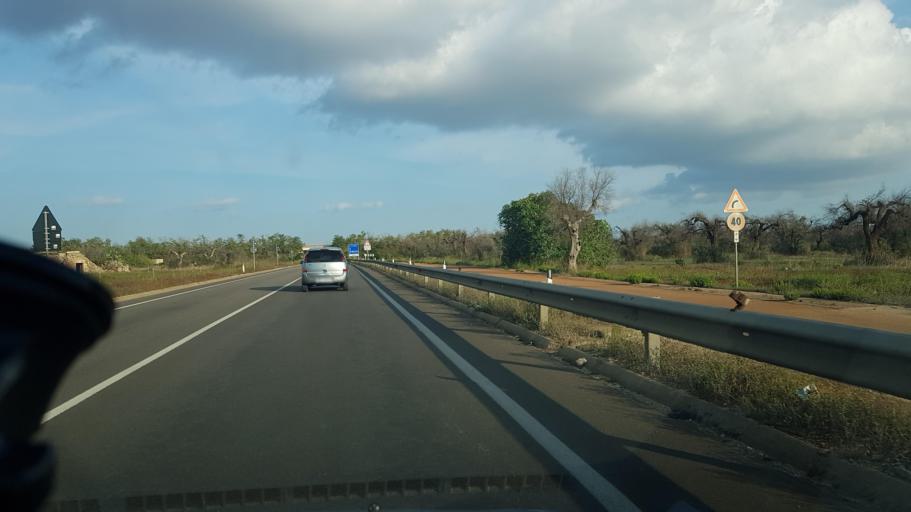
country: IT
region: Apulia
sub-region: Provincia di Lecce
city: Gemini
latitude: 39.9186
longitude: 18.2131
